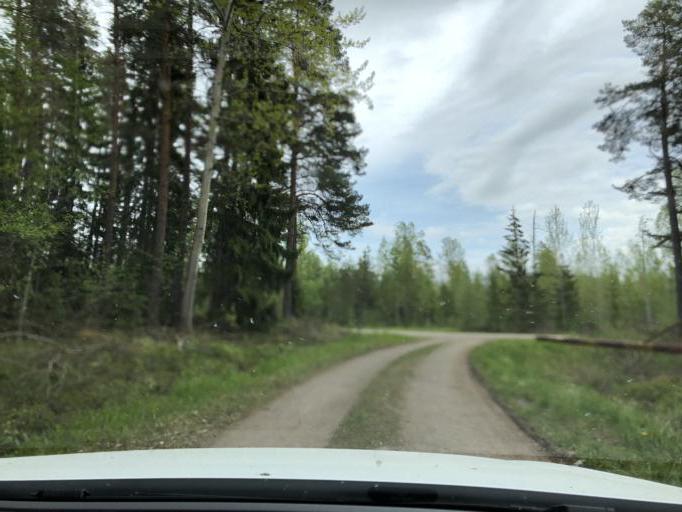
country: SE
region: Uppsala
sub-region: Heby Kommun
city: OEstervala
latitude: 60.3737
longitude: 17.2395
